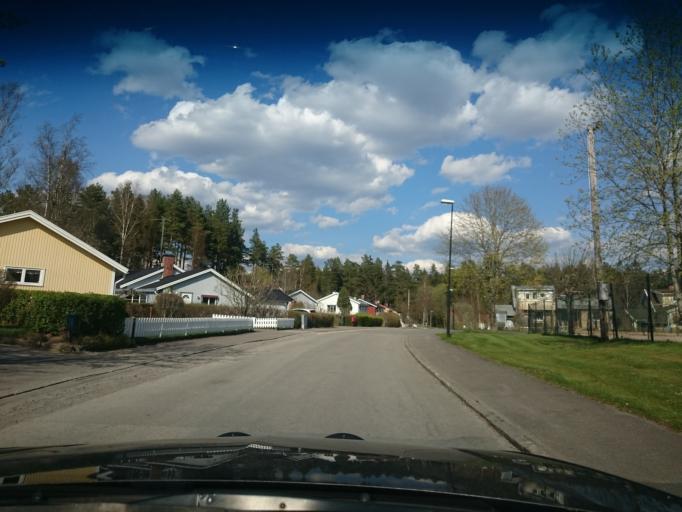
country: SE
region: Joenkoeping
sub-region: Vetlanda Kommun
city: Vetlanda
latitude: 57.4279
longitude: 15.0992
